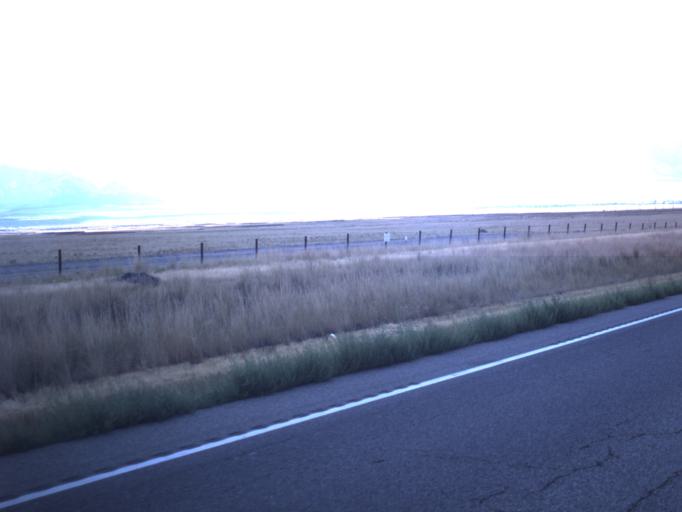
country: US
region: Utah
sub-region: Tooele County
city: Tooele
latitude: 40.5623
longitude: -112.3570
